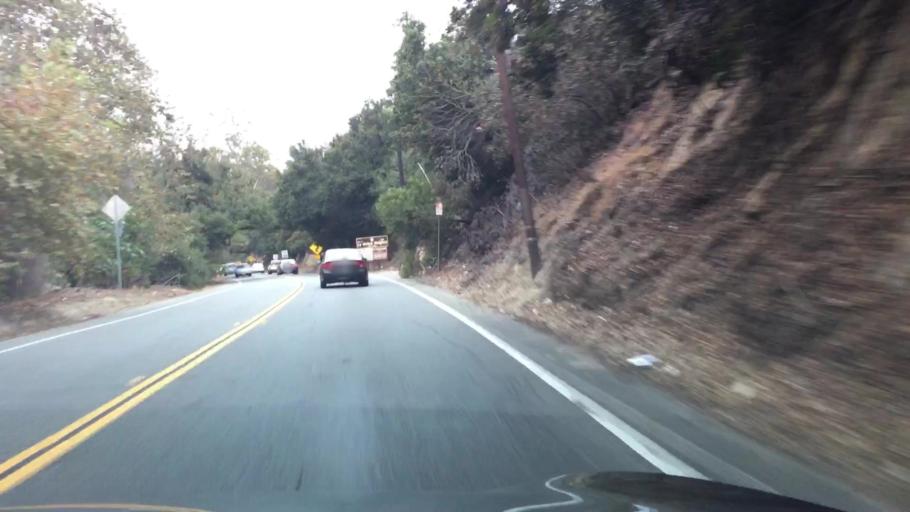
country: US
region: California
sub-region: Los Angeles County
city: Hacienda Heights
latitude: 33.9733
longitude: -117.9669
